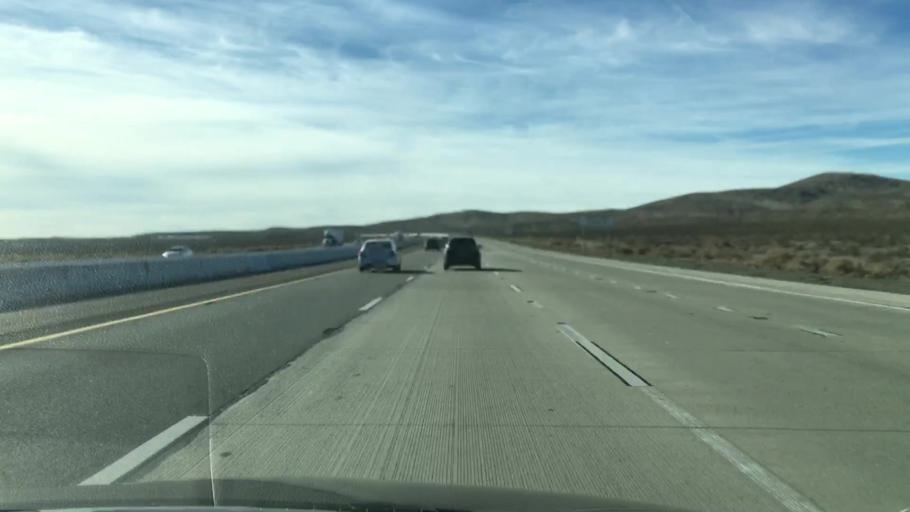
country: US
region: California
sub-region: San Bernardino County
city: Victorville
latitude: 34.6973
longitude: -117.2080
